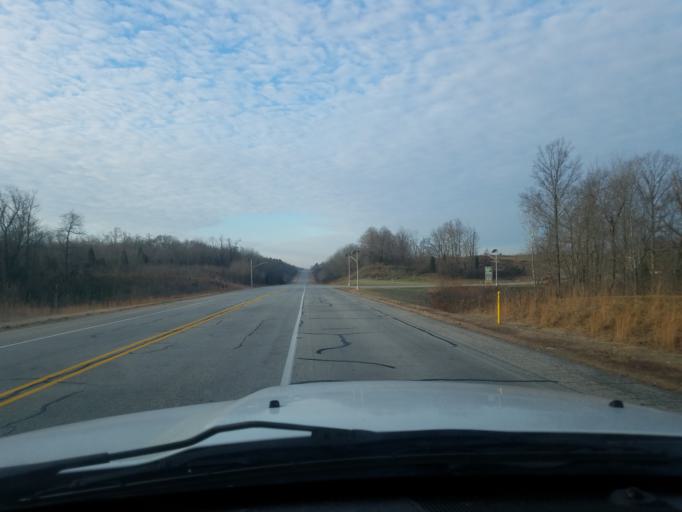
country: US
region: Indiana
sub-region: Perry County
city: Tell City
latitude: 37.9887
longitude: -86.7122
